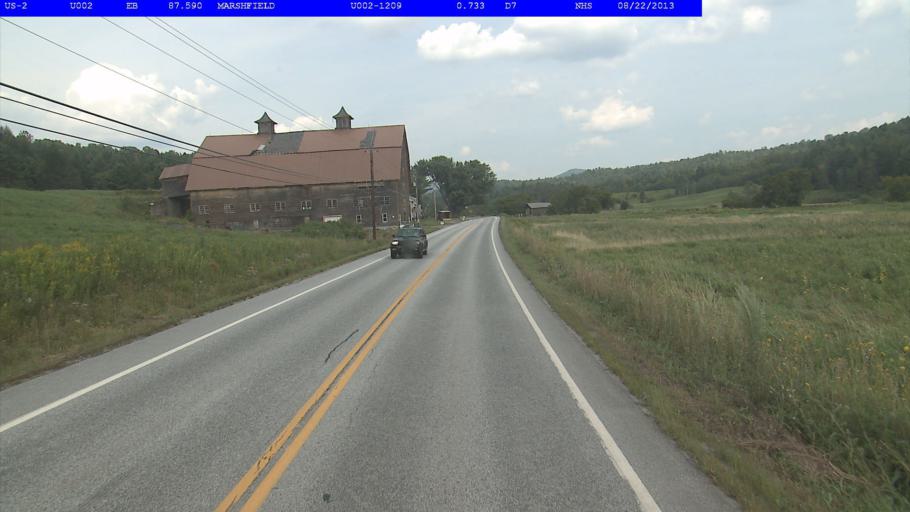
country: US
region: Vermont
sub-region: Washington County
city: Barre
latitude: 44.2867
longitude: -72.4114
